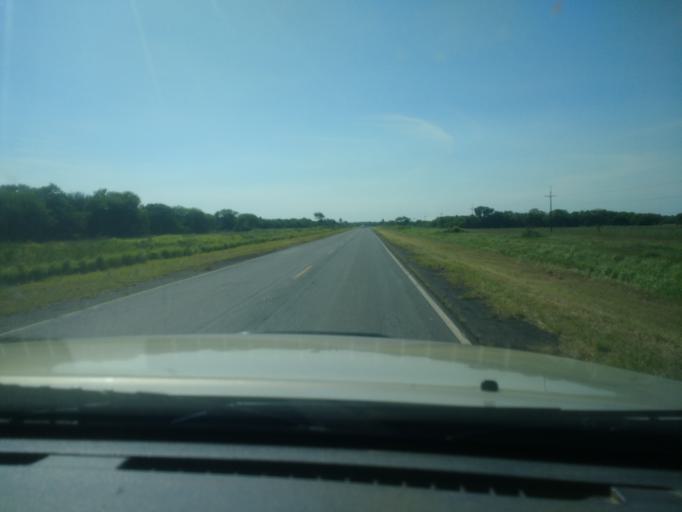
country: PY
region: Presidente Hayes
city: Benjamin Aceval
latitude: -24.9031
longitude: -57.6520
